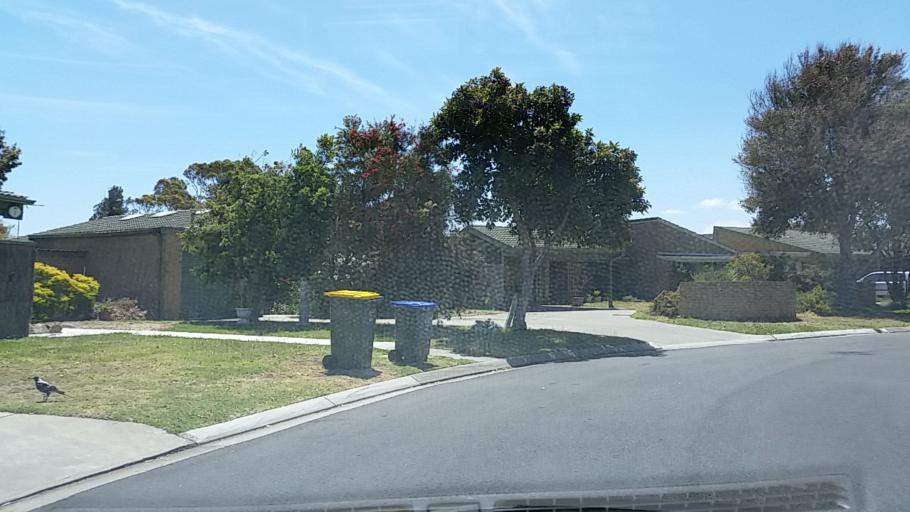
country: AU
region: South Australia
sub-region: Charles Sturt
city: Grange
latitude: -34.8979
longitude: 138.4962
